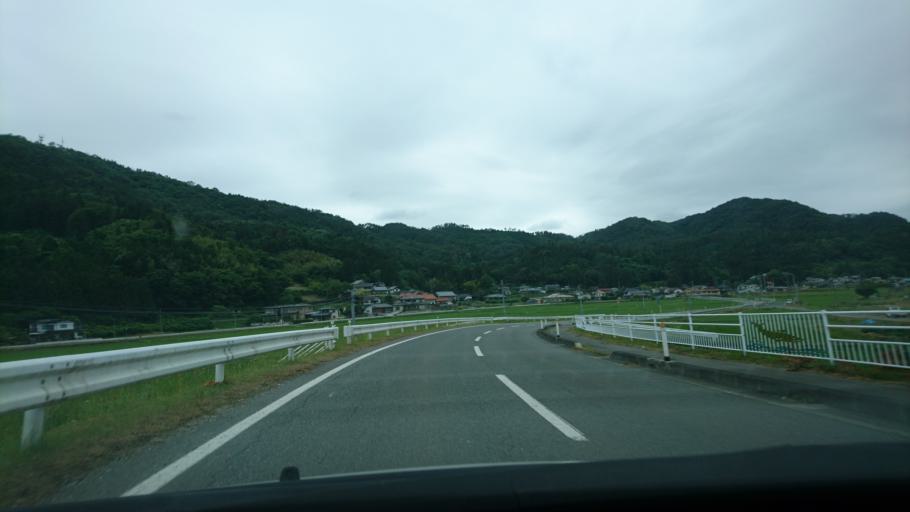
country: JP
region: Iwate
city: Ichinoseki
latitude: 38.9615
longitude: 141.2448
